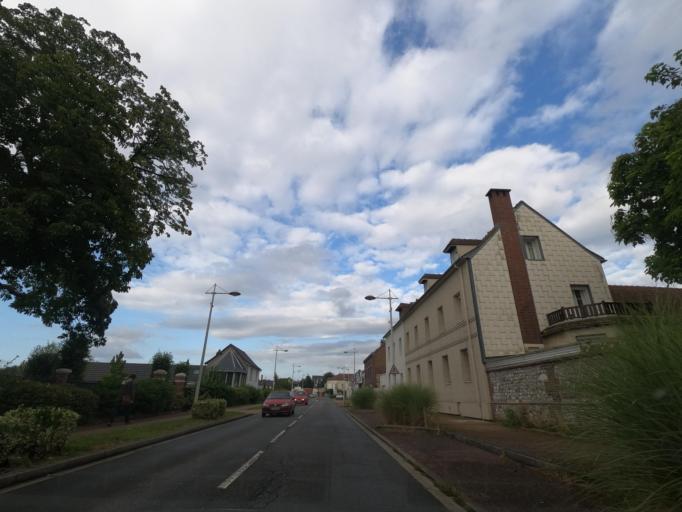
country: FR
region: Haute-Normandie
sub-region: Departement de la Seine-Maritime
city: Grand-Couronne
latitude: 49.3554
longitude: 1.0059
